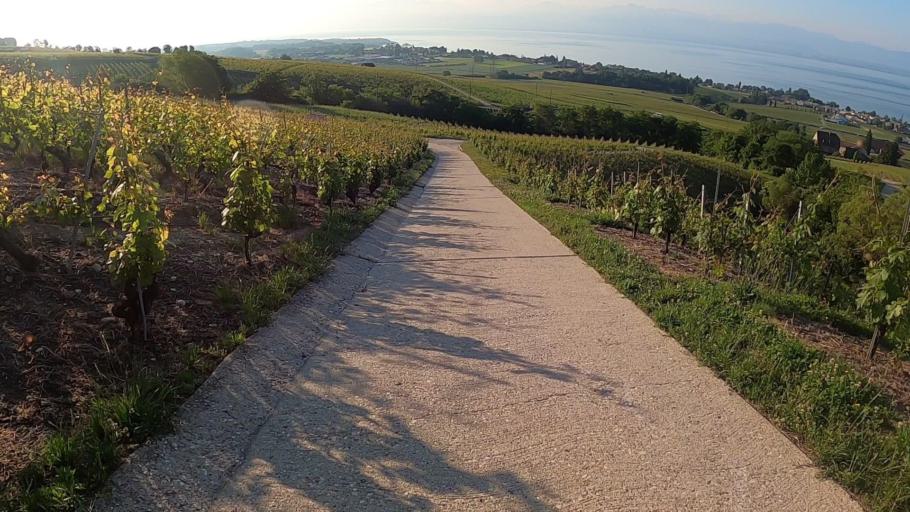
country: CH
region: Vaud
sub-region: Nyon District
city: Rolle
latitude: 46.4752
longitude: 6.3432
